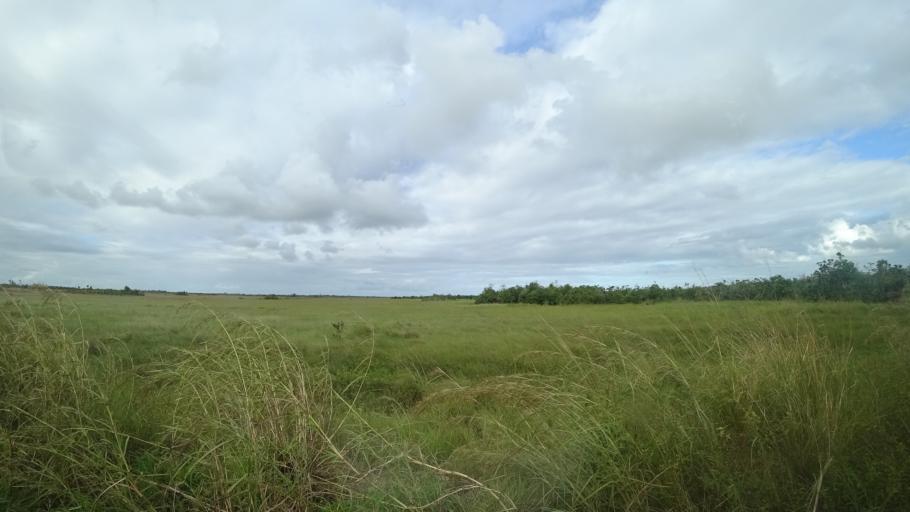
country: MZ
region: Sofala
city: Beira
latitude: -19.6287
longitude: 35.0602
